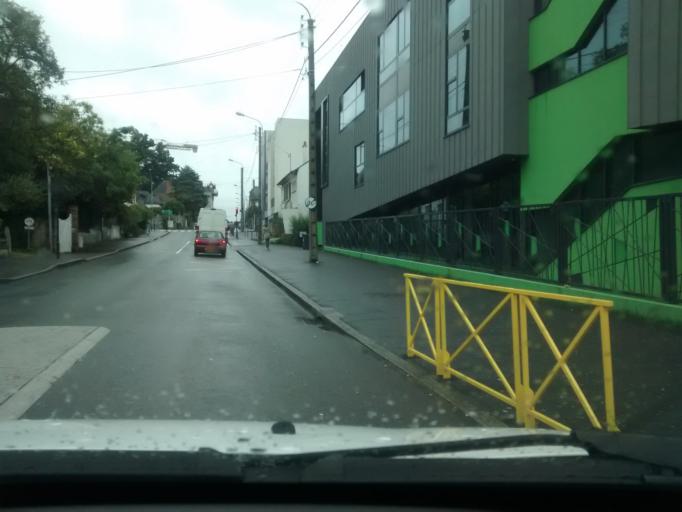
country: FR
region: Brittany
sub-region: Departement d'Ille-et-Vilaine
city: Rennes
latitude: 48.1256
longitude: -1.6682
